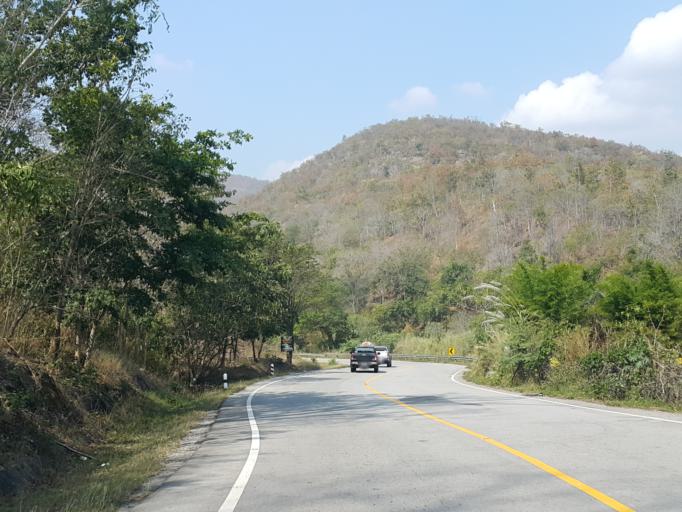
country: TH
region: Chiang Mai
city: Hot
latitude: 18.2331
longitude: 98.5492
